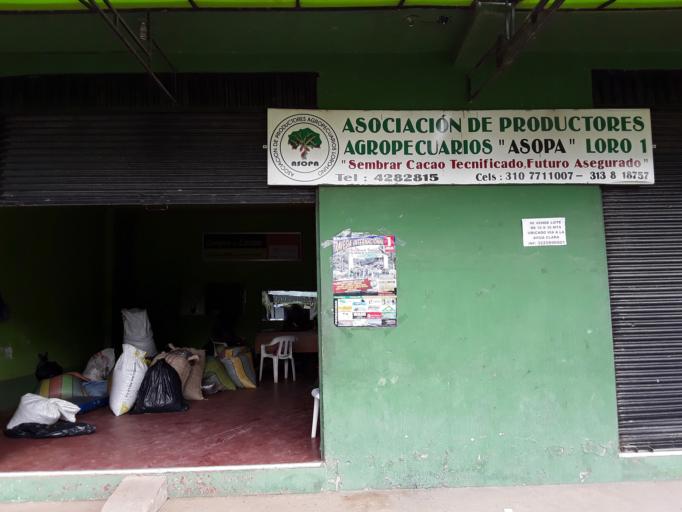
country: CO
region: Putumayo
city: San Miguel
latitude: 0.3412
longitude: -76.9120
